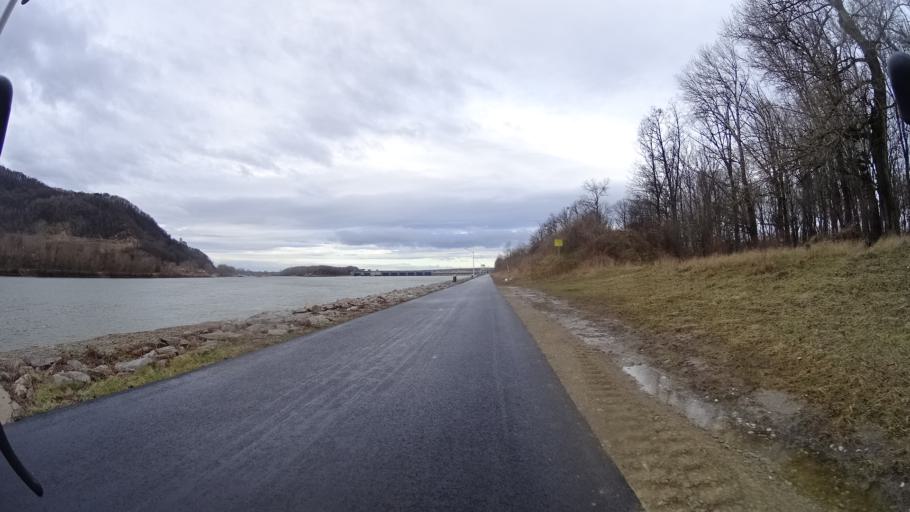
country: AT
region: Lower Austria
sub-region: Politischer Bezirk Korneuburg
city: Spillern
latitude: 48.3550
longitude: 16.2630
